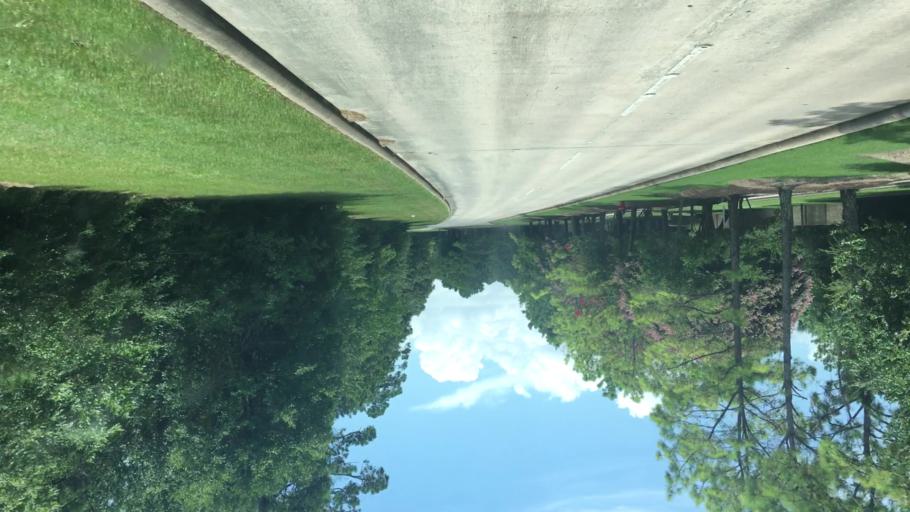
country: US
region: Texas
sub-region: Harris County
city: Atascocita
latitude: 29.9842
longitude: -95.1910
